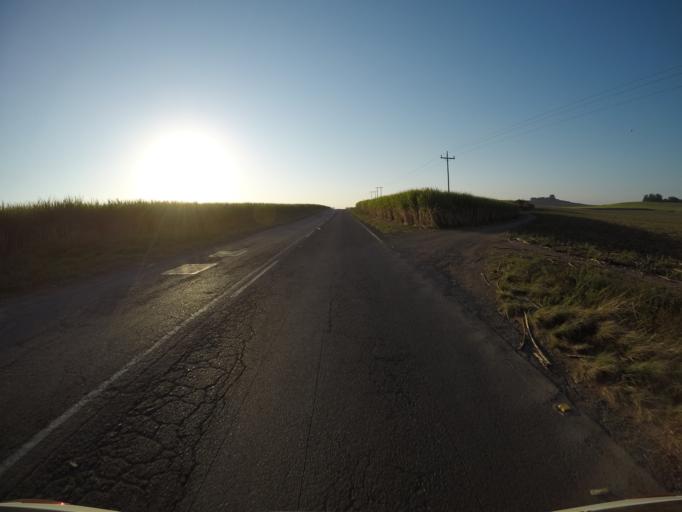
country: ZA
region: KwaZulu-Natal
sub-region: uThungulu District Municipality
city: eSikhawini
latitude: -28.9485
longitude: 31.7236
